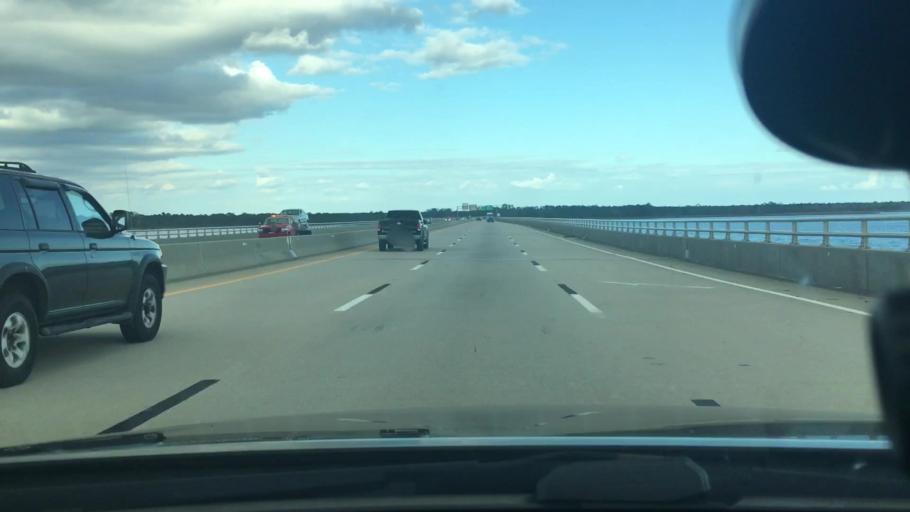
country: US
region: North Carolina
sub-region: Craven County
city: James City
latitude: 35.0974
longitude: -77.0249
